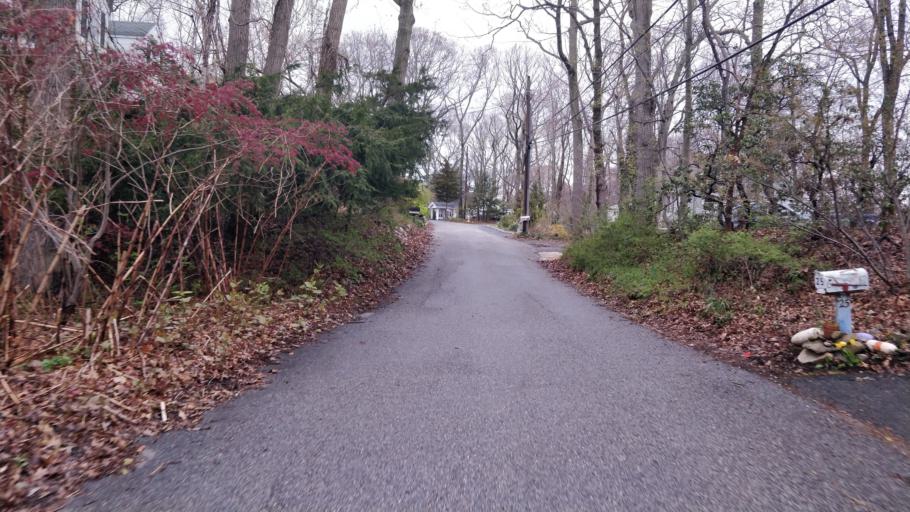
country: US
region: New York
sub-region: Suffolk County
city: Port Jefferson
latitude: 40.9519
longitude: -73.0860
